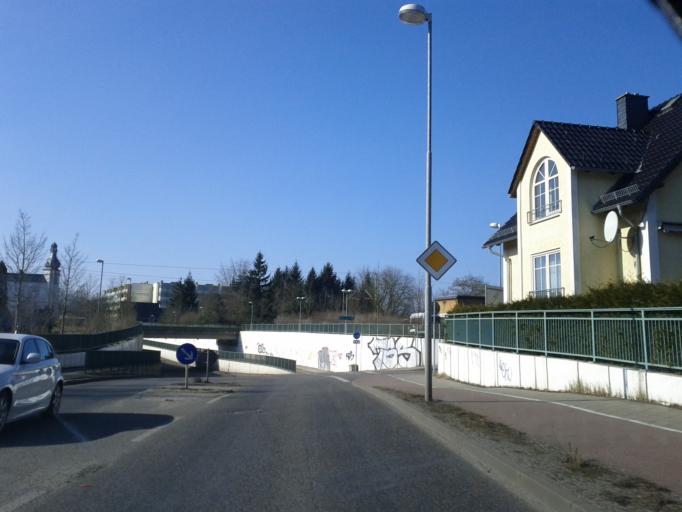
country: DE
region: Brandenburg
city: Erkner
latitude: 52.4210
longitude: 13.7596
